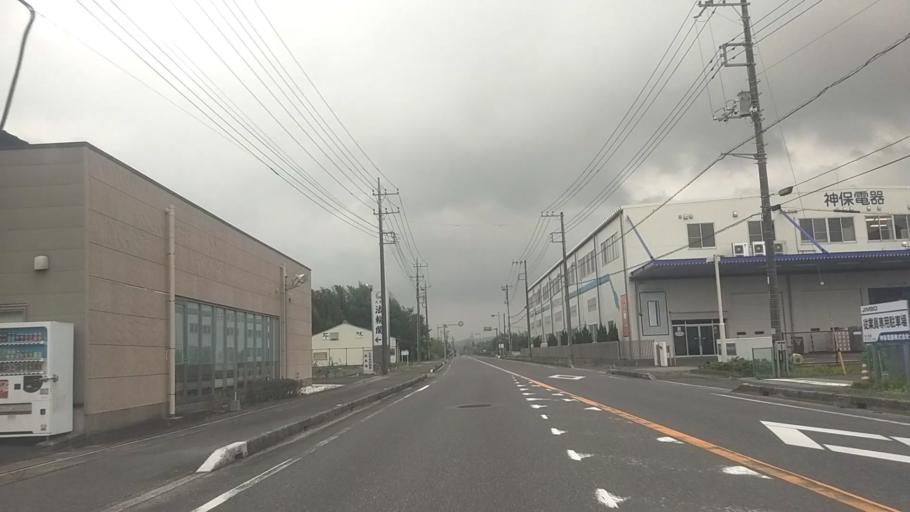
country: JP
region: Chiba
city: Ohara
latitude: 35.2863
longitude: 140.2637
